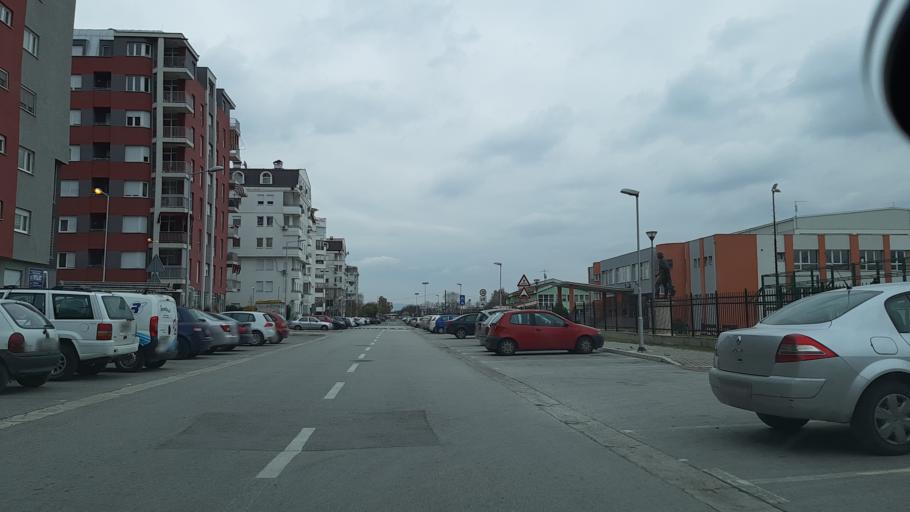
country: MK
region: Kisela Voda
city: Usje
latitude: 41.9800
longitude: 21.4706
